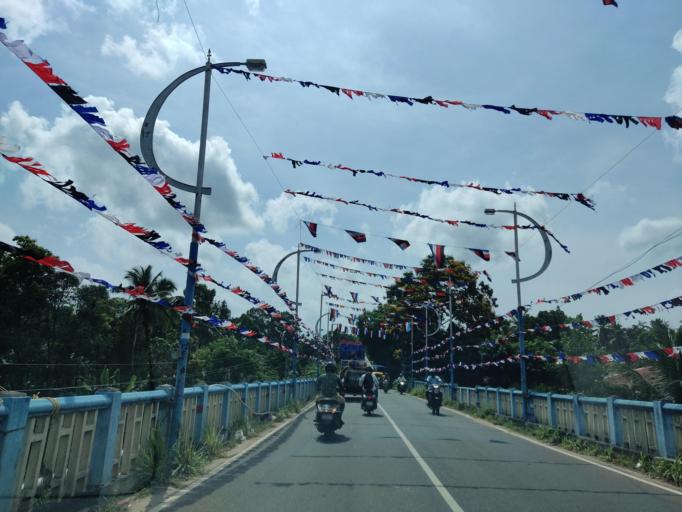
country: IN
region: Kerala
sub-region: Alappuzha
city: Mavelikara
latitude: 9.2631
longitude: 76.5422
